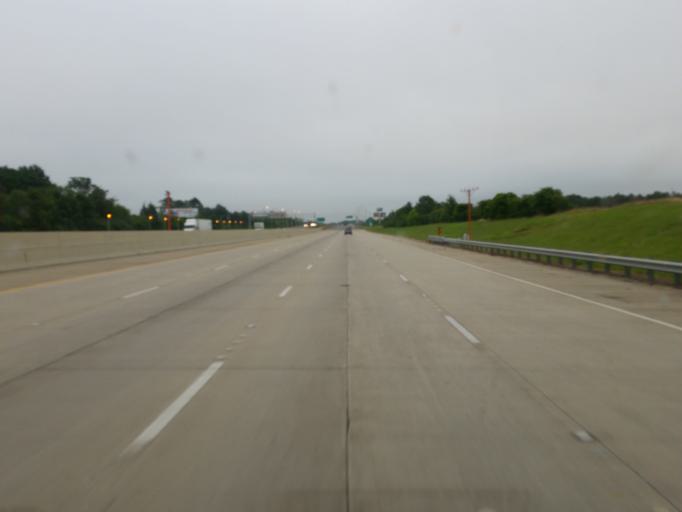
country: US
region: Louisiana
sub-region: Caddo Parish
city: Shreveport
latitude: 32.4577
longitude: -93.8393
